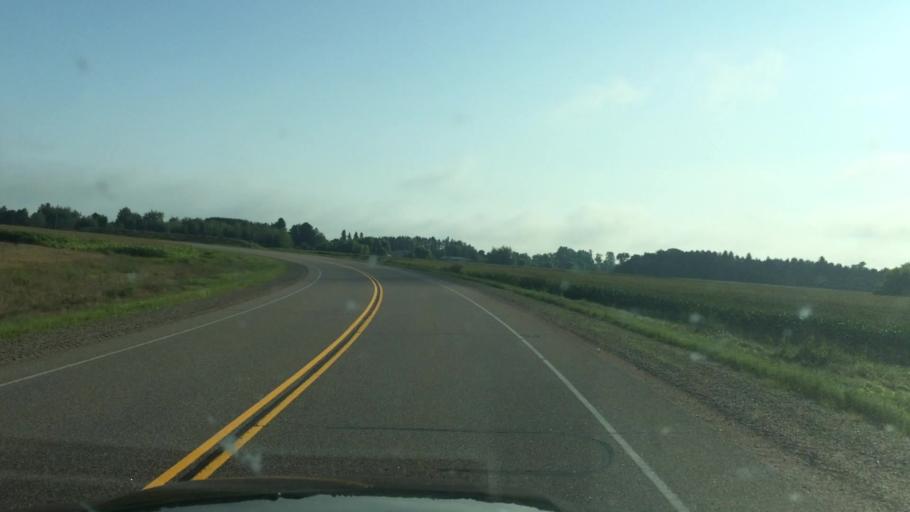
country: US
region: Wisconsin
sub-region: Langlade County
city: Antigo
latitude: 45.1429
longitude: -89.1864
